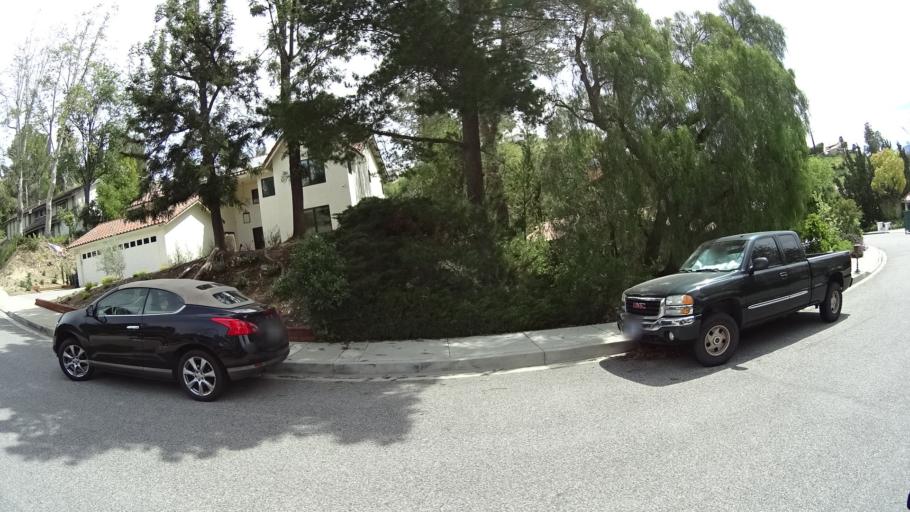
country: US
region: California
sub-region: Ventura County
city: Thousand Oaks
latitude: 34.1527
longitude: -118.8518
